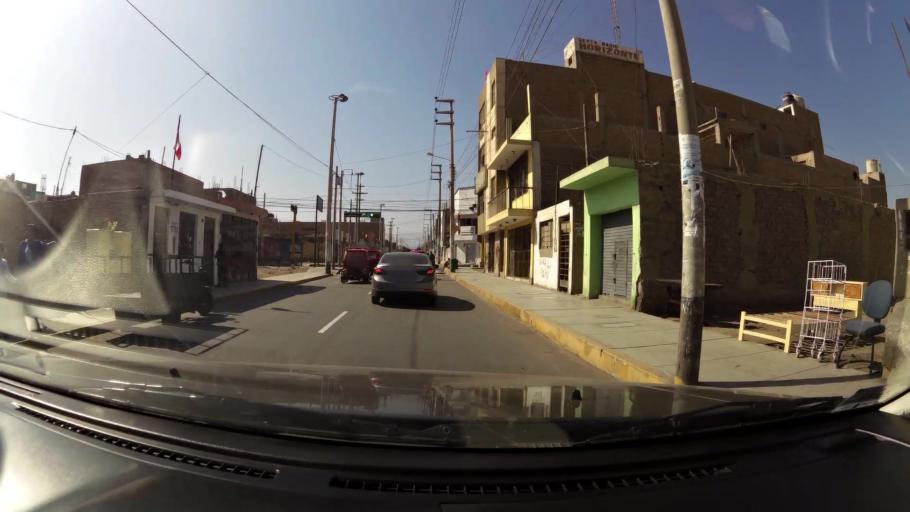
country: PE
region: Ica
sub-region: Provincia de Chincha
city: Chincha Alta
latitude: -13.4156
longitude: -76.1314
